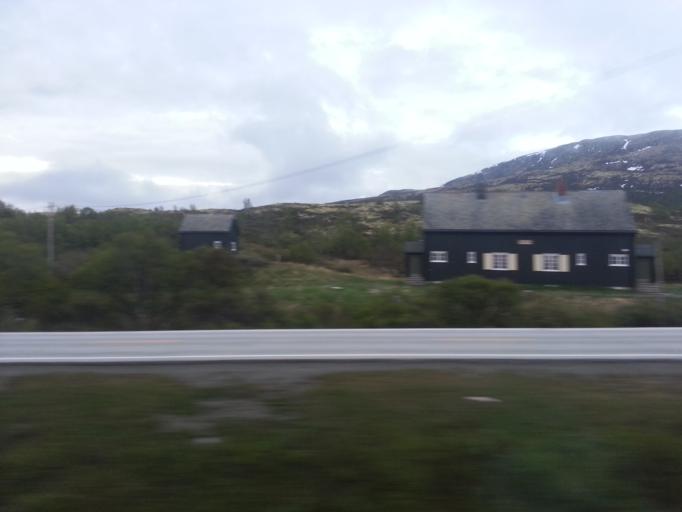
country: NO
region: Sor-Trondelag
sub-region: Oppdal
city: Oppdal
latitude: 62.2619
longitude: 9.5601
